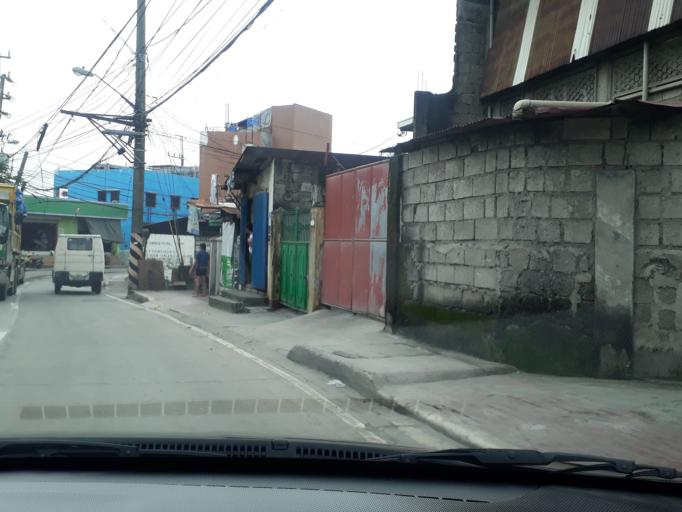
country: PH
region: Calabarzon
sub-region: Province of Rizal
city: Valenzuela
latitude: 14.7161
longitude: 120.9794
